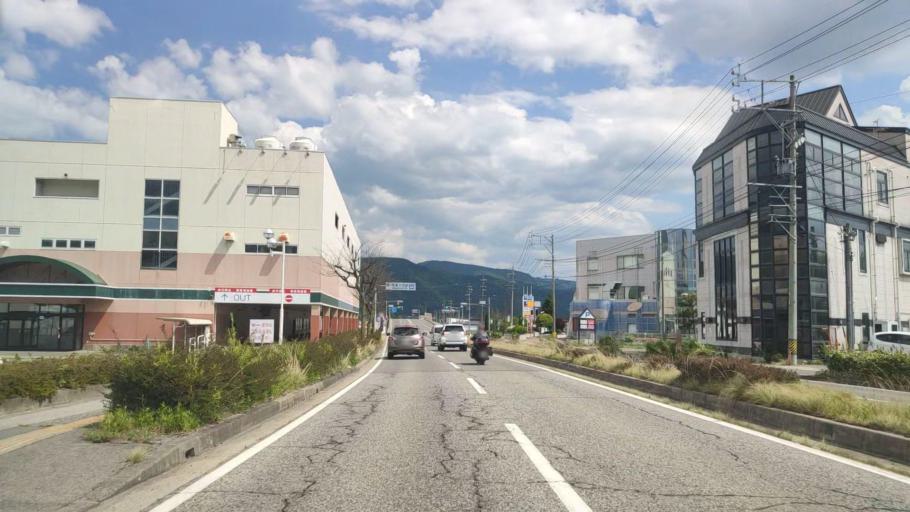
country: JP
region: Nagano
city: Omachi
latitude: 36.5001
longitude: 137.8575
